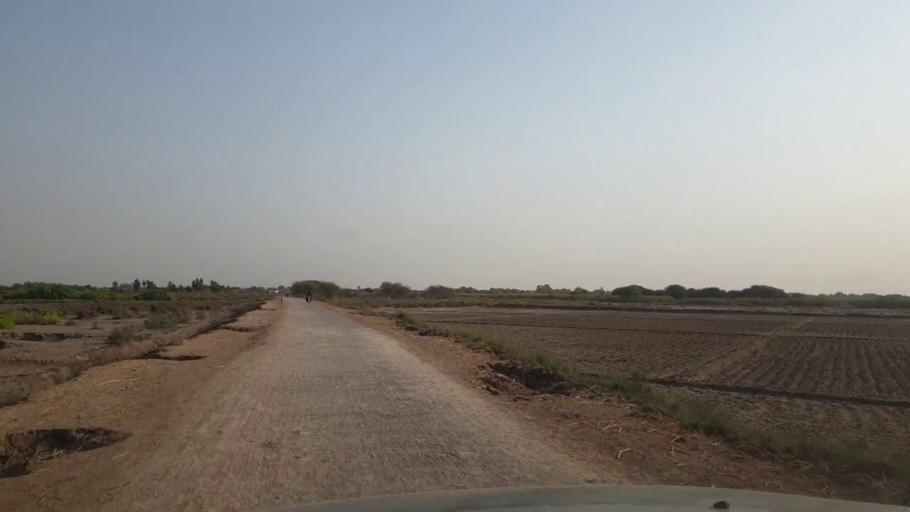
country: PK
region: Sindh
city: Bulri
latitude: 24.9503
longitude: 68.3415
